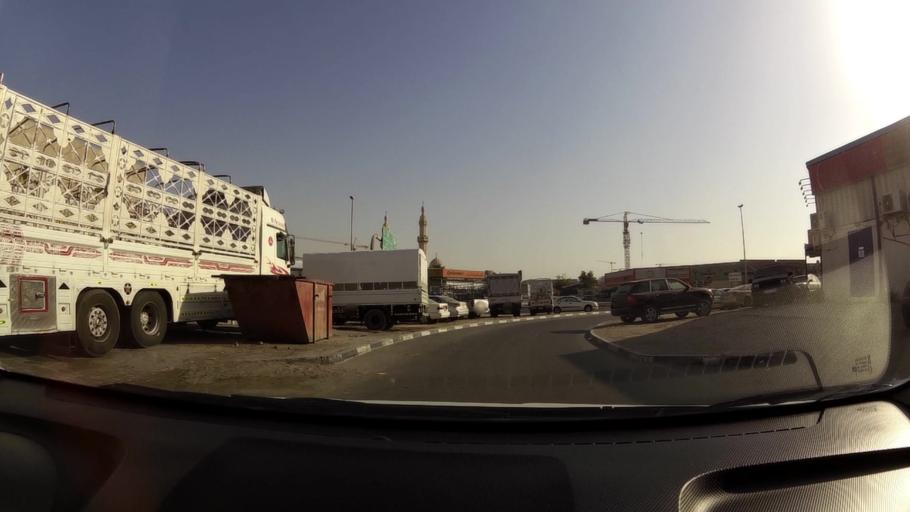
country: AE
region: Ash Shariqah
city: Sharjah
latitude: 25.2861
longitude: 55.3885
